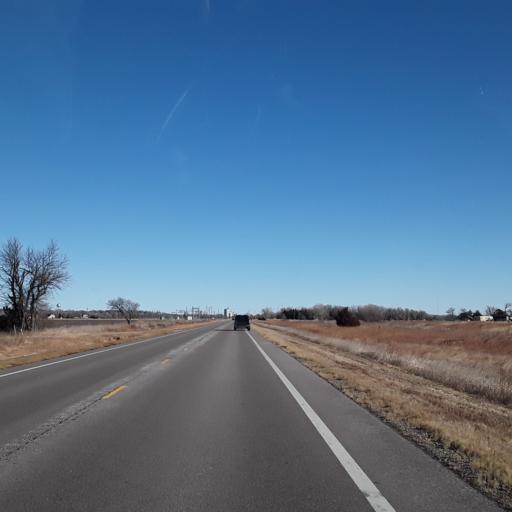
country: US
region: Kansas
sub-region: Pawnee County
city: Larned
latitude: 38.1547
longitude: -99.1291
